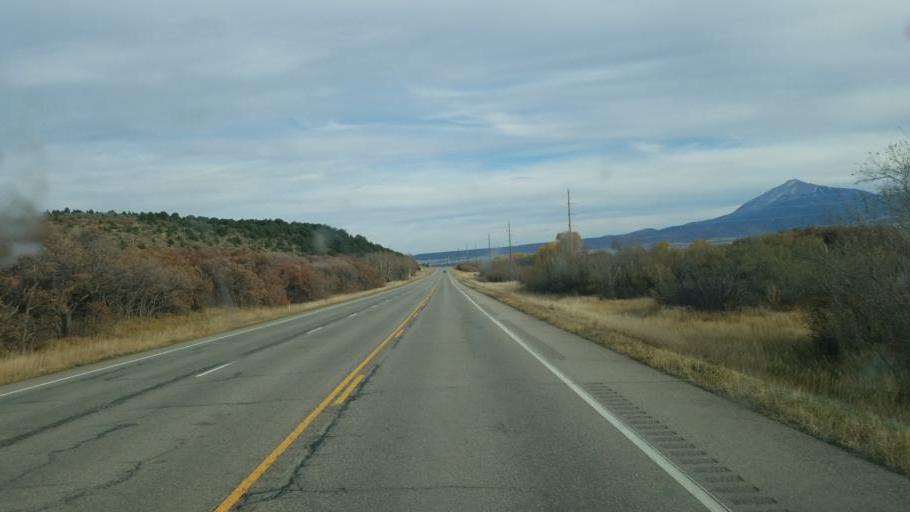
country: US
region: Colorado
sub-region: Huerfano County
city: Walsenburg
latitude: 37.5489
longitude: -105.0967
